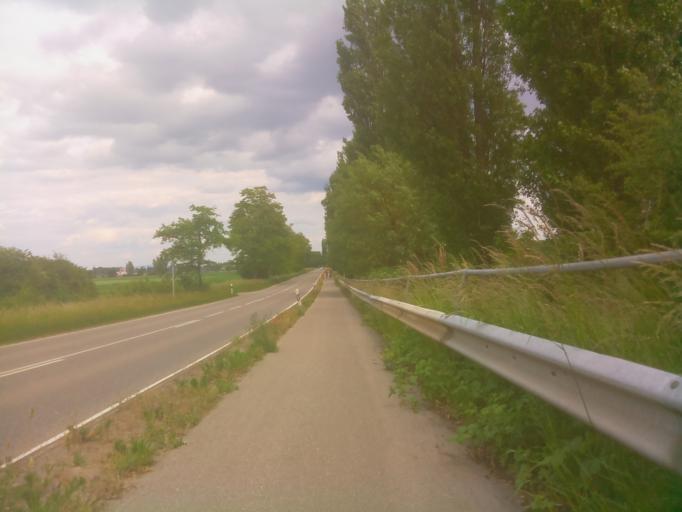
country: DE
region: Rheinland-Pfalz
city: Hessheim
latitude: 49.5258
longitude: 8.3151
